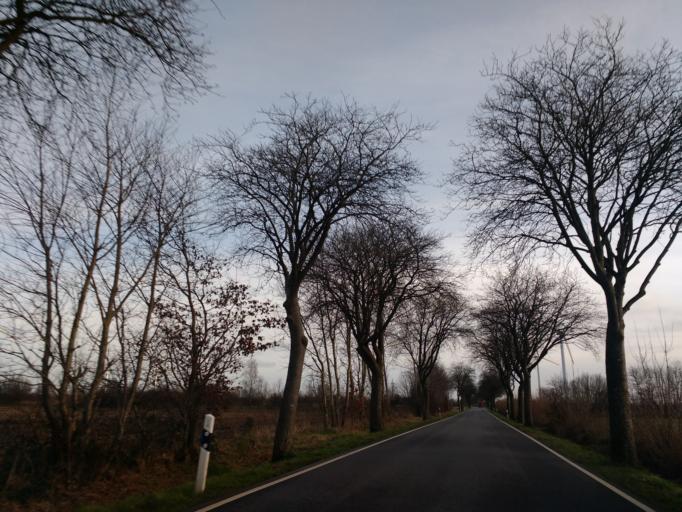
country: DE
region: Schleswig-Holstein
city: Nortorf
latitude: 54.1380
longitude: 9.8532
